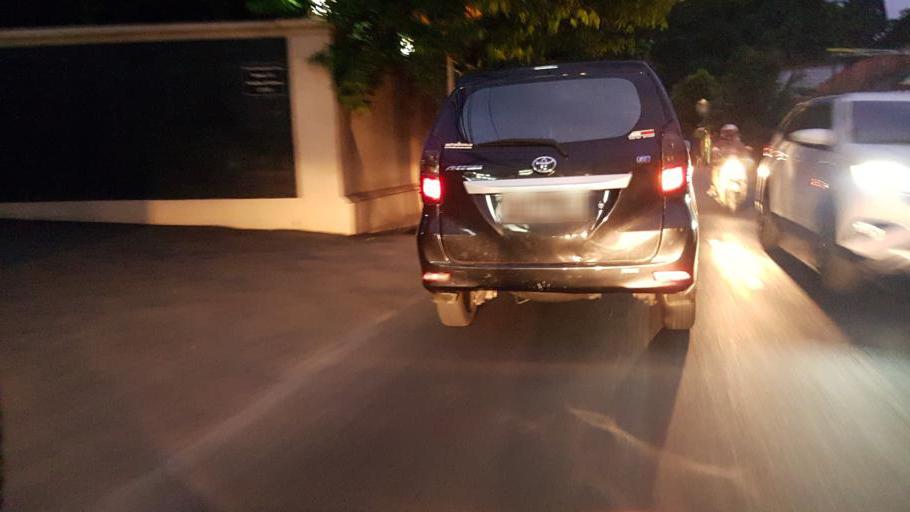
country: ID
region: Jakarta Raya
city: Jakarta
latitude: -6.3024
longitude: 106.8264
